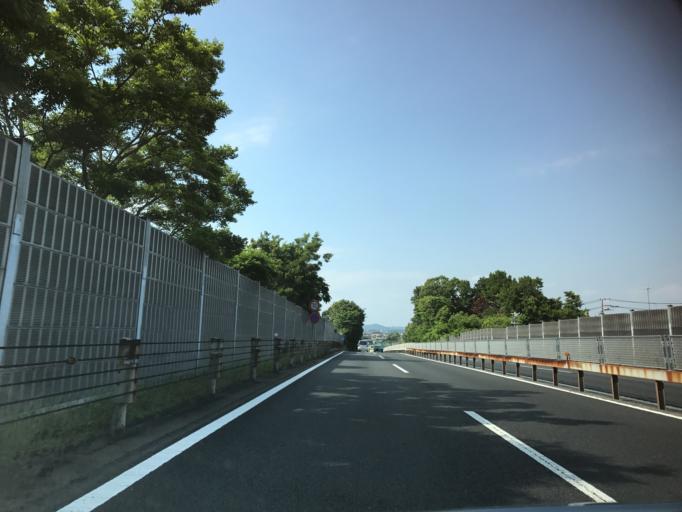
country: JP
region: Kanagawa
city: Oiso
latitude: 35.3433
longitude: 139.2966
